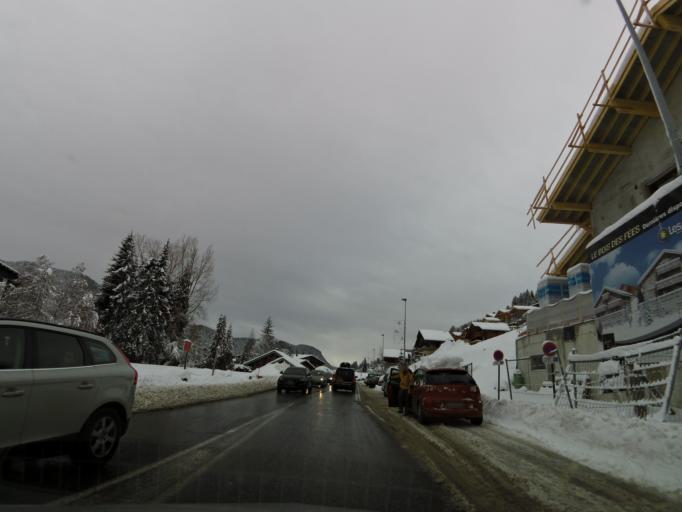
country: FR
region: Rhone-Alpes
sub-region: Departement de la Haute-Savoie
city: Les Gets
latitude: 46.1562
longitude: 6.6640
